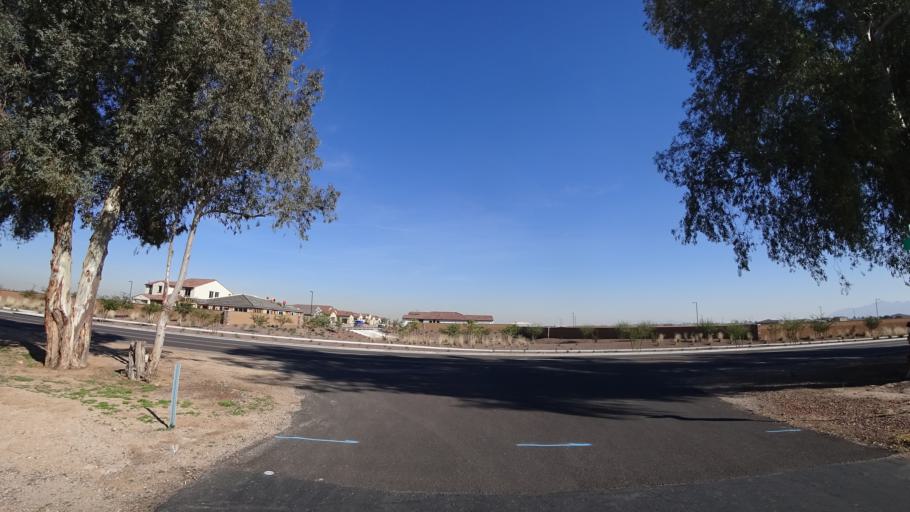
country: US
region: Arizona
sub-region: Maricopa County
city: Citrus Park
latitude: 33.5054
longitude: -112.4617
